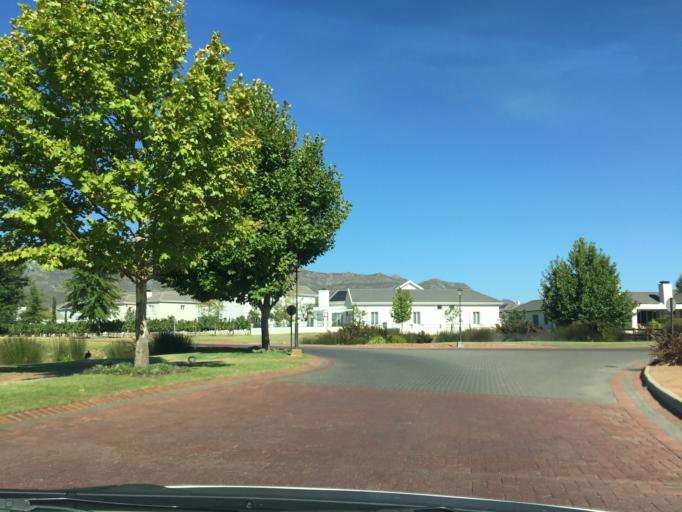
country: ZA
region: Western Cape
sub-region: Cape Winelands District Municipality
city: Paarl
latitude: -33.8008
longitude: 18.9700
